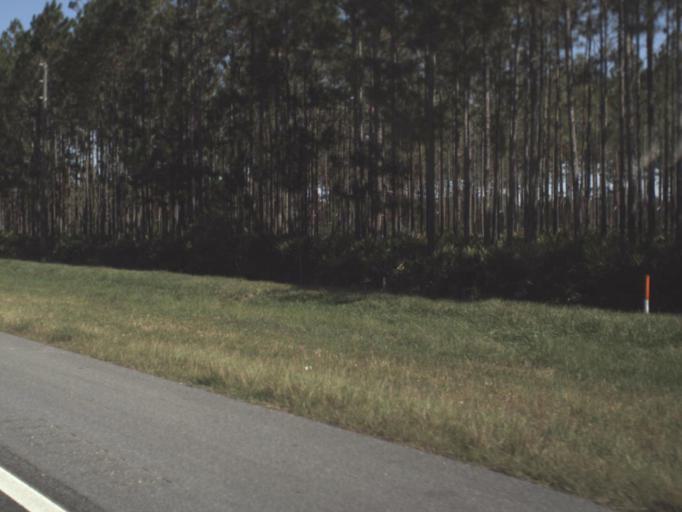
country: US
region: Florida
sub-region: Pasco County
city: Odessa
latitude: 28.2182
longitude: -82.5491
